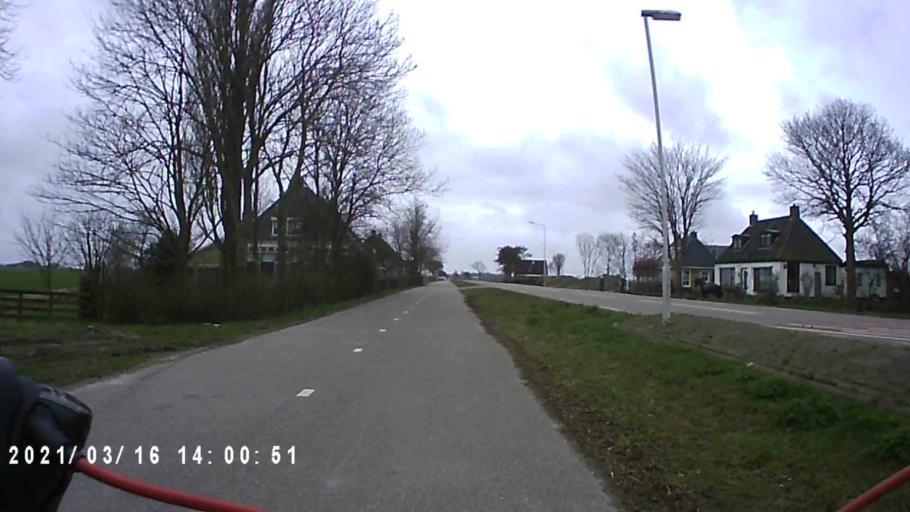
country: NL
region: Friesland
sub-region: Gemeente Franekeradeel
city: Sexbierum
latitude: 53.1844
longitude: 5.4907
